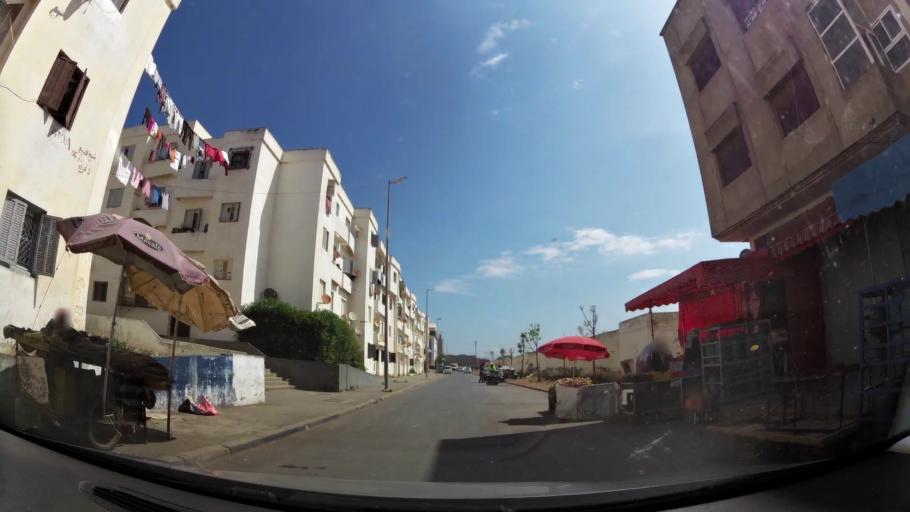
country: MA
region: Rabat-Sale-Zemmour-Zaer
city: Sale
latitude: 34.0763
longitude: -6.7950
